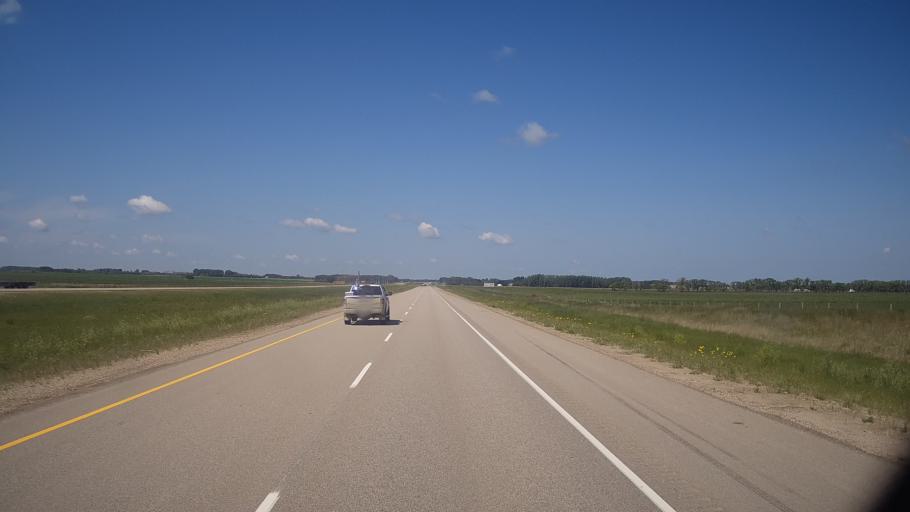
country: CA
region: Saskatchewan
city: Saskatoon
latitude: 52.0123
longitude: -106.3697
